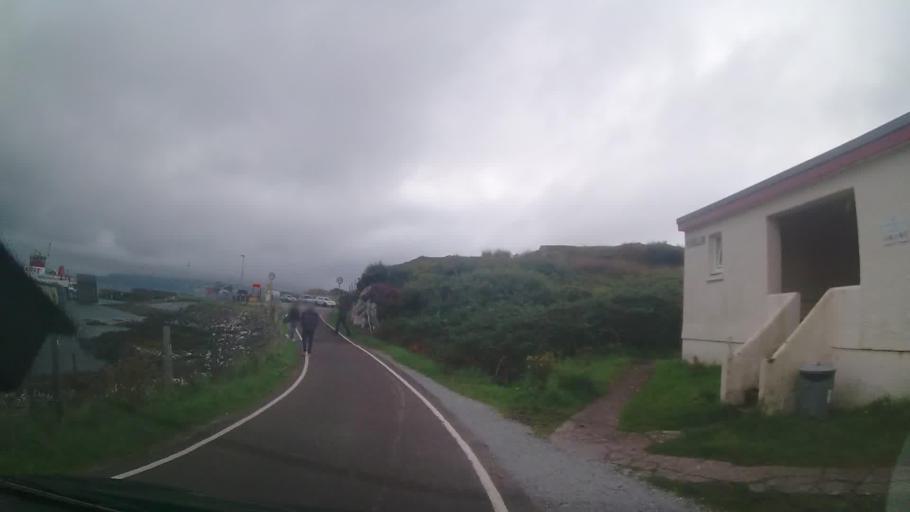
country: GB
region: Scotland
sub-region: Argyll and Bute
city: Isle Of Mull
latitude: 56.6893
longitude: -6.0960
